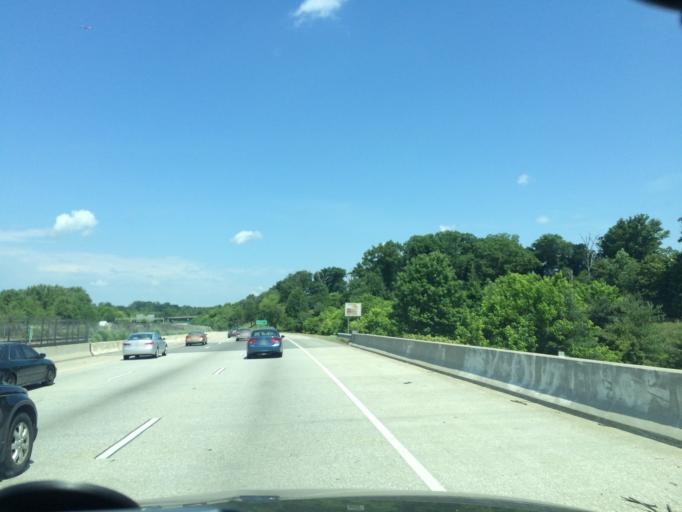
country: US
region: Maryland
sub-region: Baltimore County
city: Garrison
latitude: 39.3836
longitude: -76.7551
